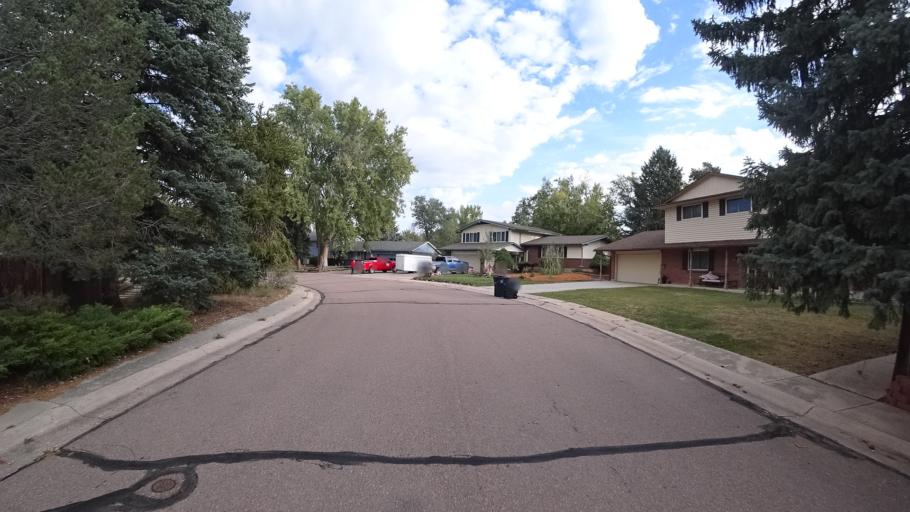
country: US
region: Colorado
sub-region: El Paso County
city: Cimarron Hills
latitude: 38.8646
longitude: -104.7521
